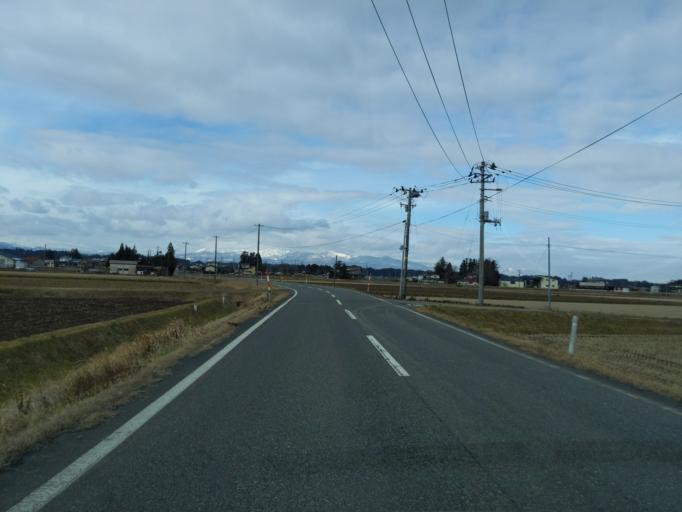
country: JP
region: Iwate
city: Mizusawa
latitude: 39.0875
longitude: 141.1613
